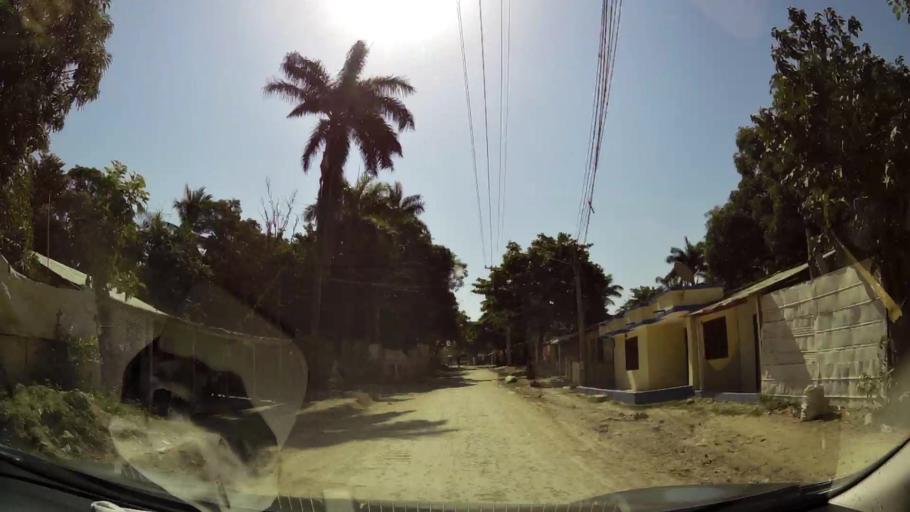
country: CO
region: Bolivar
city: Cartagena
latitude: 10.3678
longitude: -75.4925
